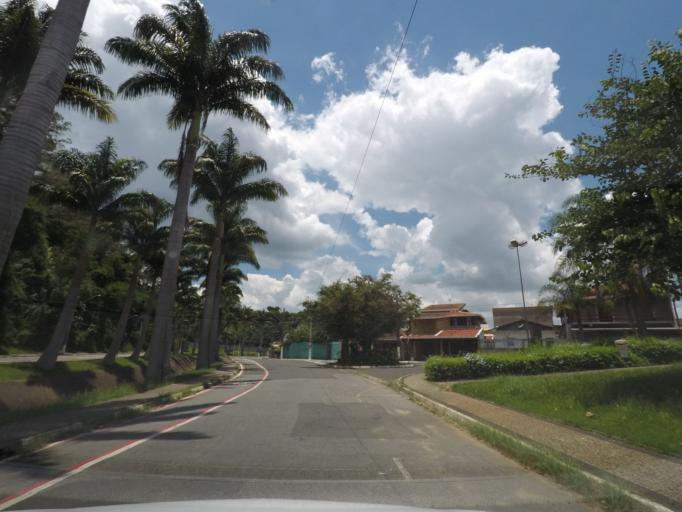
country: BR
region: Sao Paulo
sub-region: Vinhedo
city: Vinhedo
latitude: -23.0266
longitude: -46.9720
